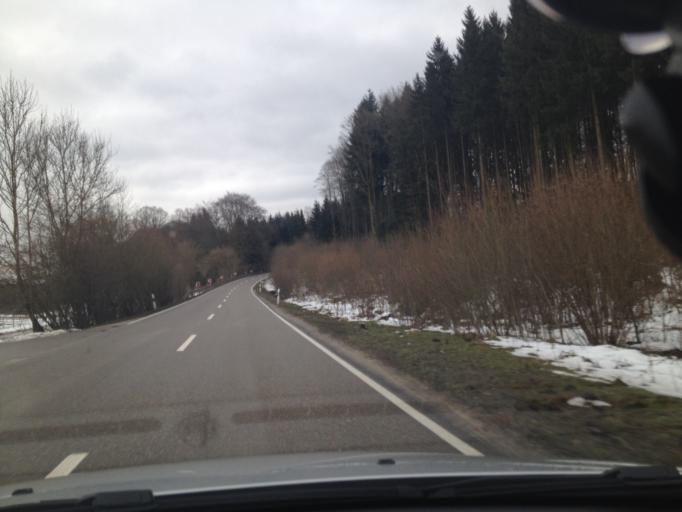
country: DE
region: Bavaria
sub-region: Swabia
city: Aystetten
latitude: 48.4036
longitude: 10.7557
